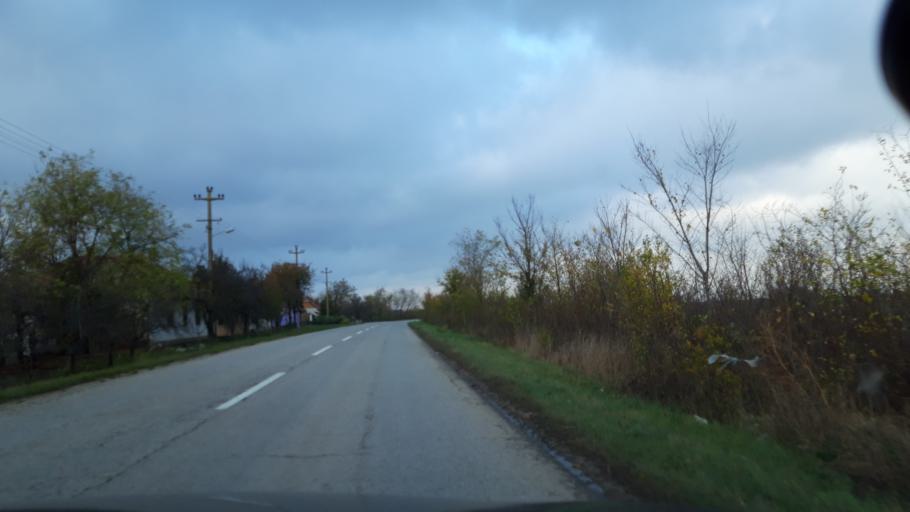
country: RS
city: Sanad
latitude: 45.9838
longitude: 20.1114
